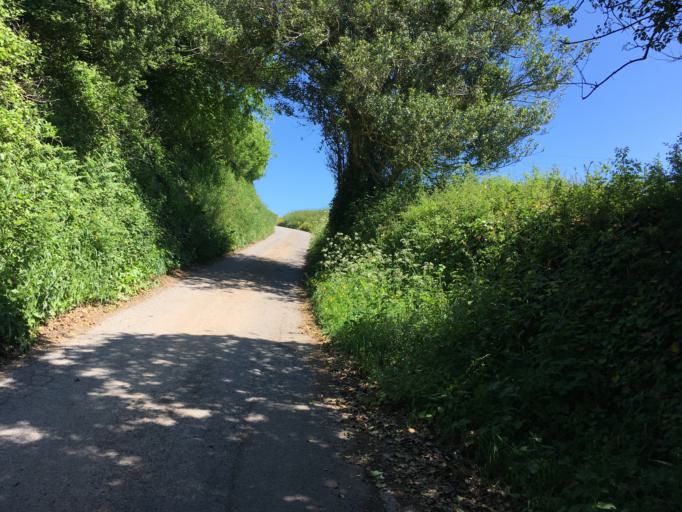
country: GB
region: England
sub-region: Devon
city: Dartmouth
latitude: 50.3466
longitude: -3.5442
